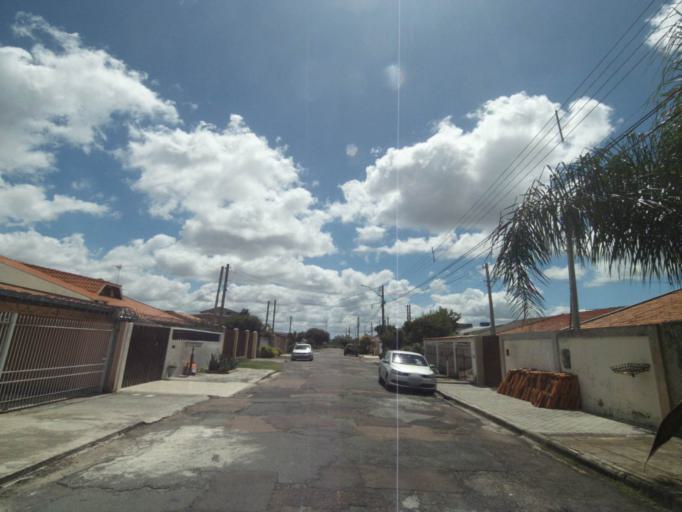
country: BR
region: Parana
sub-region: Pinhais
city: Pinhais
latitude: -25.4416
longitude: -49.2037
